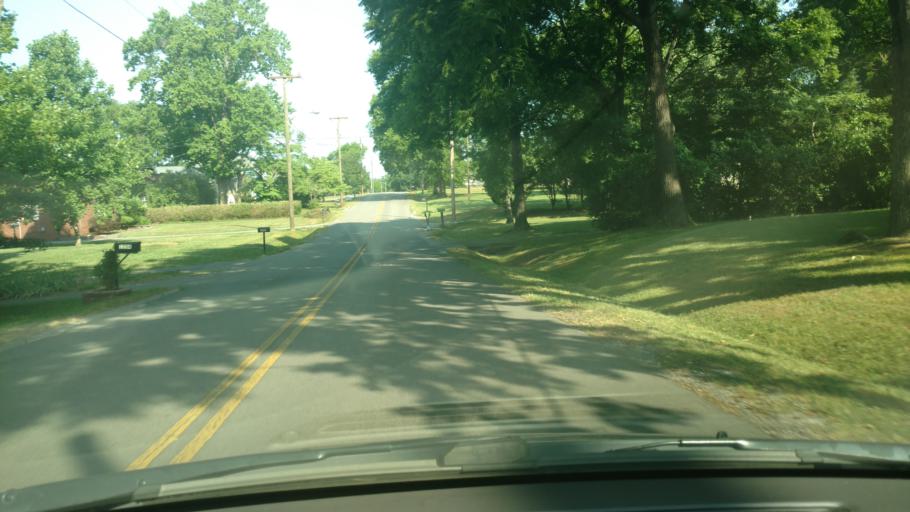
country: US
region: Tennessee
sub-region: Davidson County
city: Nashville
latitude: 36.2199
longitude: -86.7184
